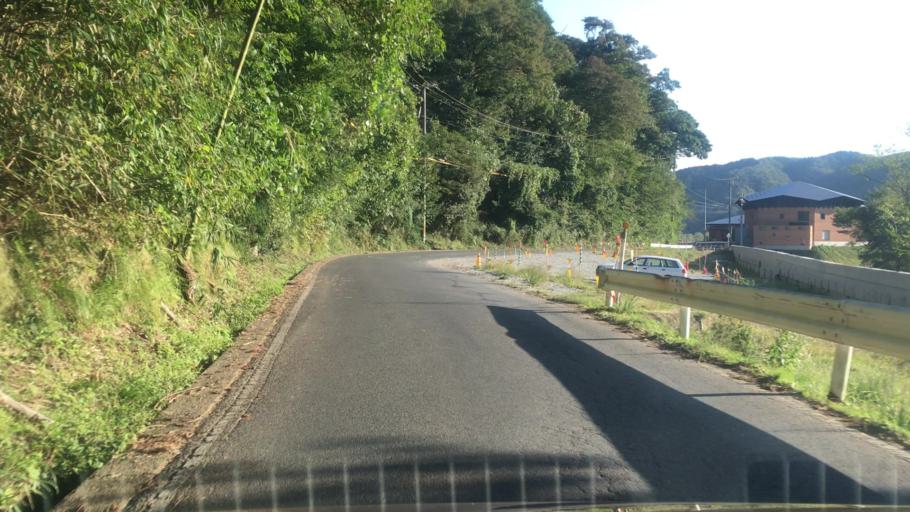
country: JP
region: Hyogo
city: Toyooka
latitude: 35.5911
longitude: 134.8040
